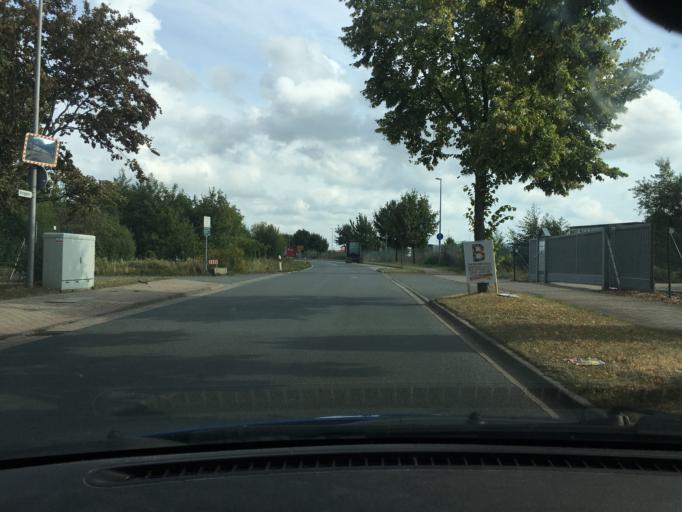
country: DE
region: Lower Saxony
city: Grossgoltern
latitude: 52.3071
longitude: 9.4922
